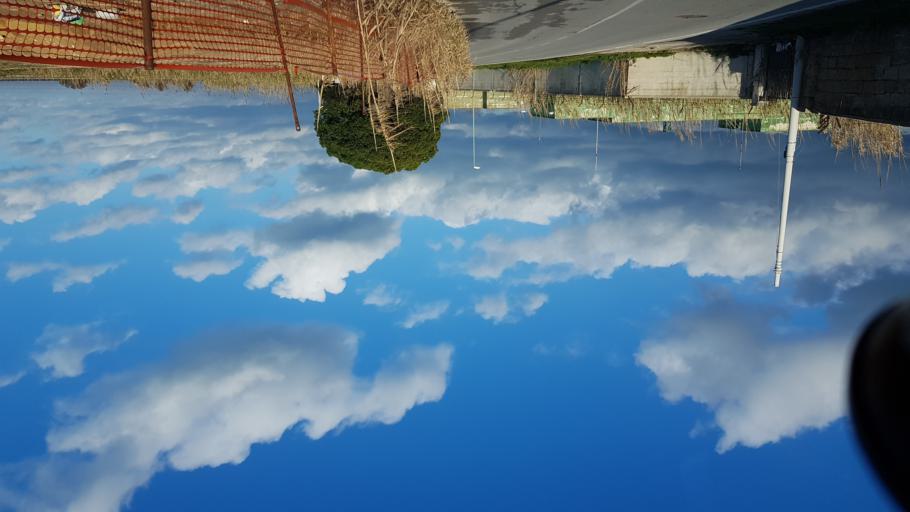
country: IT
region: Apulia
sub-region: Provincia di Brindisi
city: Materdomini
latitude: 40.6604
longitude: 17.9577
